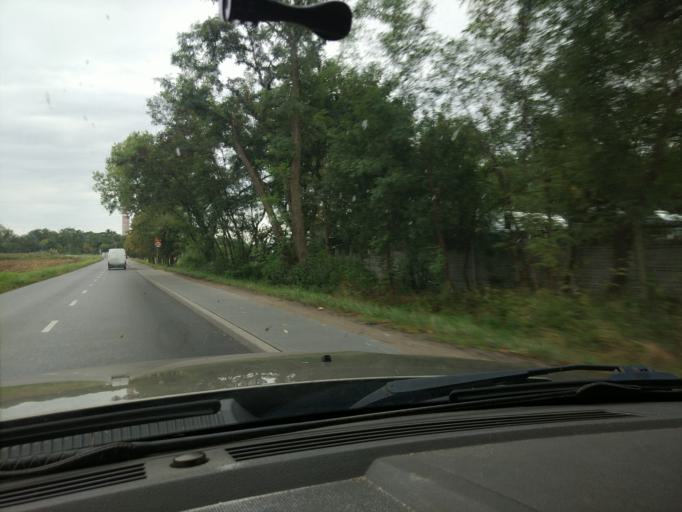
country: PL
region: Masovian Voivodeship
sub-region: Powiat warszawski zachodni
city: Ozarow Mazowiecki
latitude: 52.1882
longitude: 20.7526
